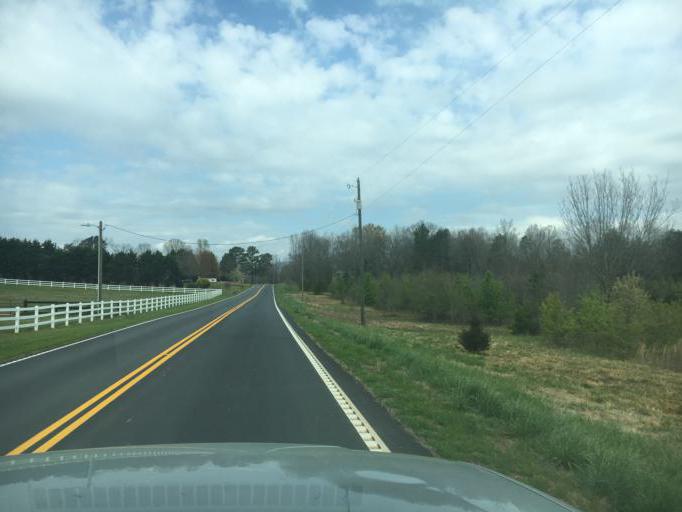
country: US
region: South Carolina
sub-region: Spartanburg County
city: Landrum
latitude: 35.0932
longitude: -82.2007
